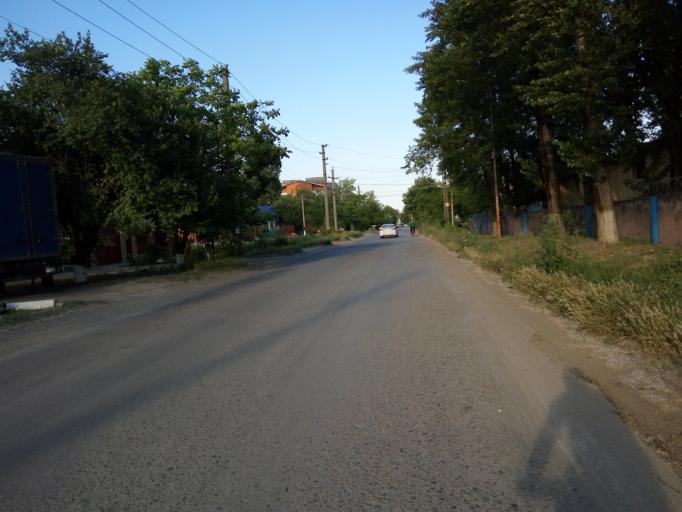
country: RU
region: Rostov
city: Bataysk
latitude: 47.1151
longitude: 39.7369
